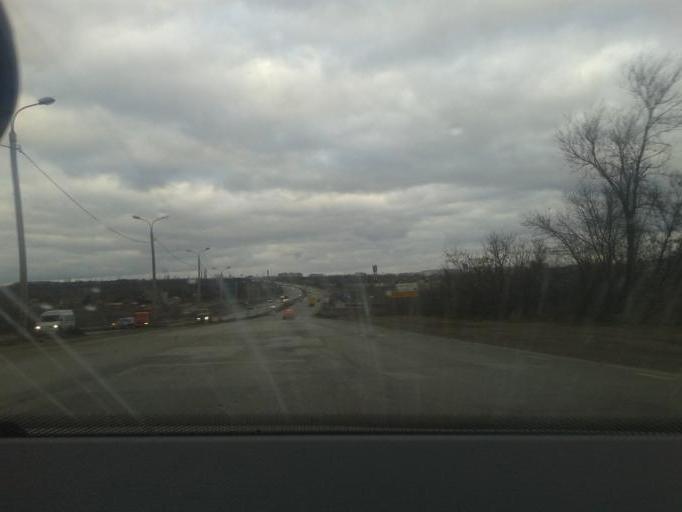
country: RU
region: Volgograd
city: Volgograd
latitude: 48.7288
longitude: 44.4501
